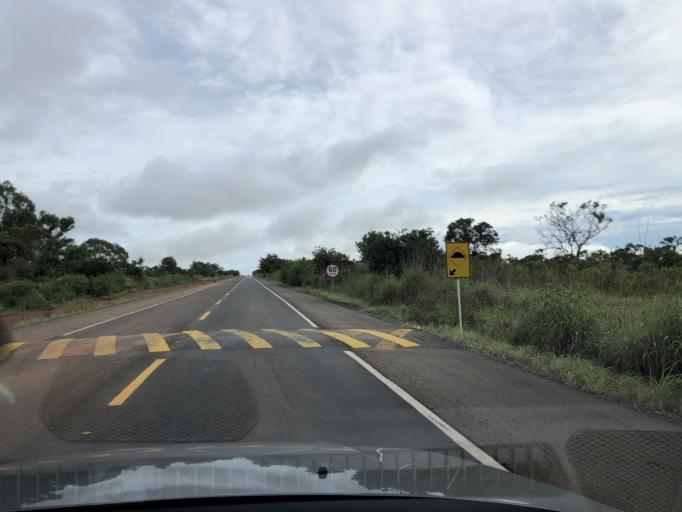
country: BR
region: Federal District
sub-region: Brasilia
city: Brasilia
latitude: -15.6449
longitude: -48.0803
